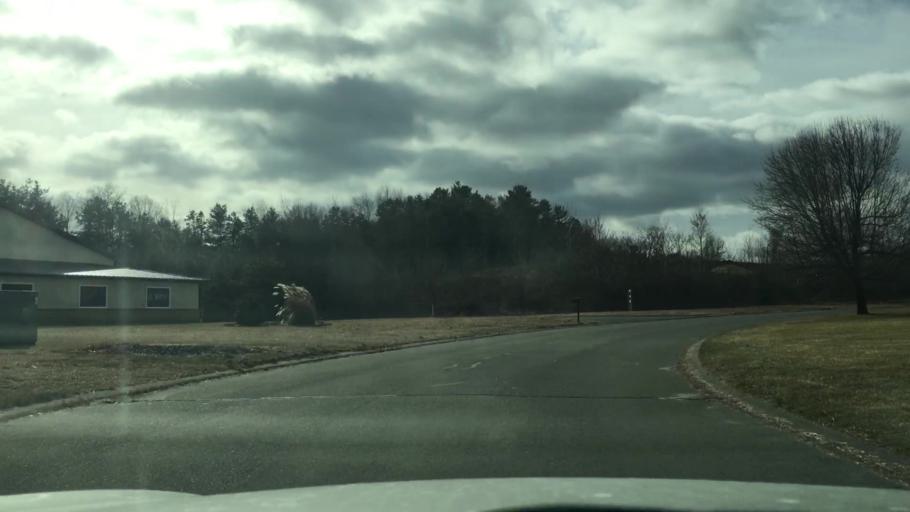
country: US
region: Massachusetts
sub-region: Hampden County
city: Southwick
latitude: 42.0691
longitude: -72.7412
